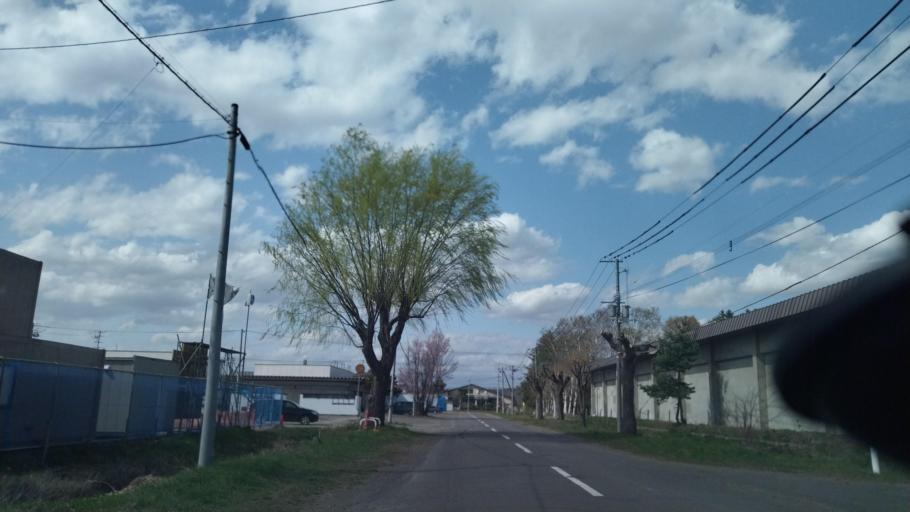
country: JP
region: Hokkaido
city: Obihiro
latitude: 42.9305
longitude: 143.1354
